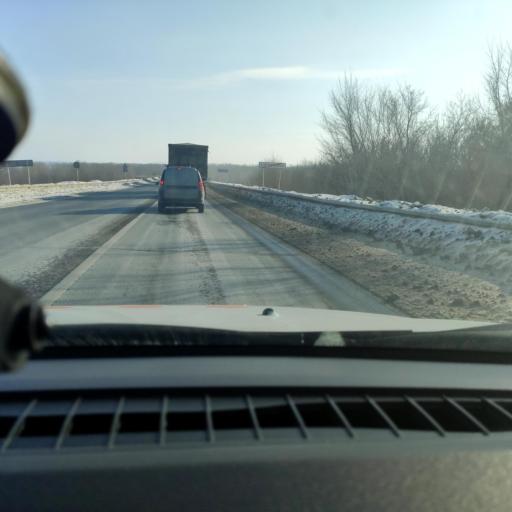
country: RU
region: Samara
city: Smyshlyayevka
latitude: 53.2368
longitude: 50.4853
